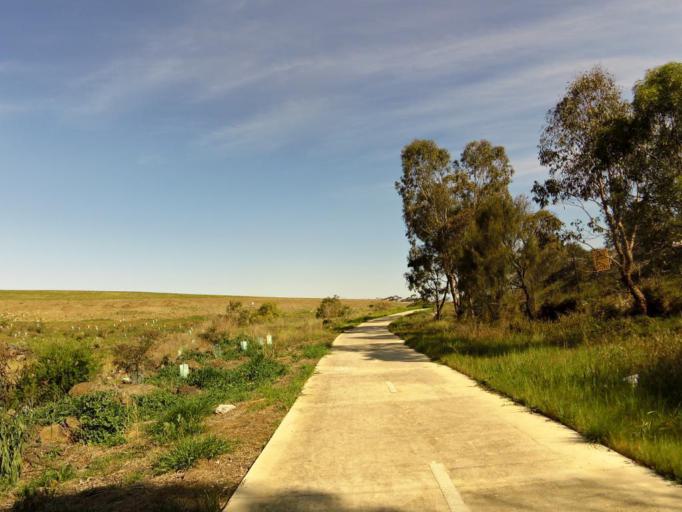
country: AU
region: Victoria
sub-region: Brimbank
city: Brooklyn
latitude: -37.8105
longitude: 144.8287
